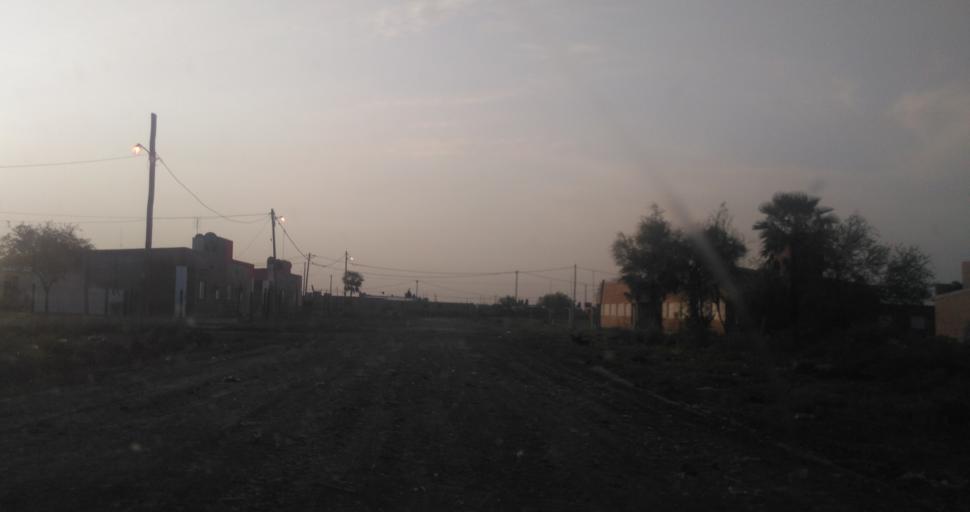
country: AR
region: Chaco
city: Resistencia
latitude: -27.4727
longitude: -59.0214
